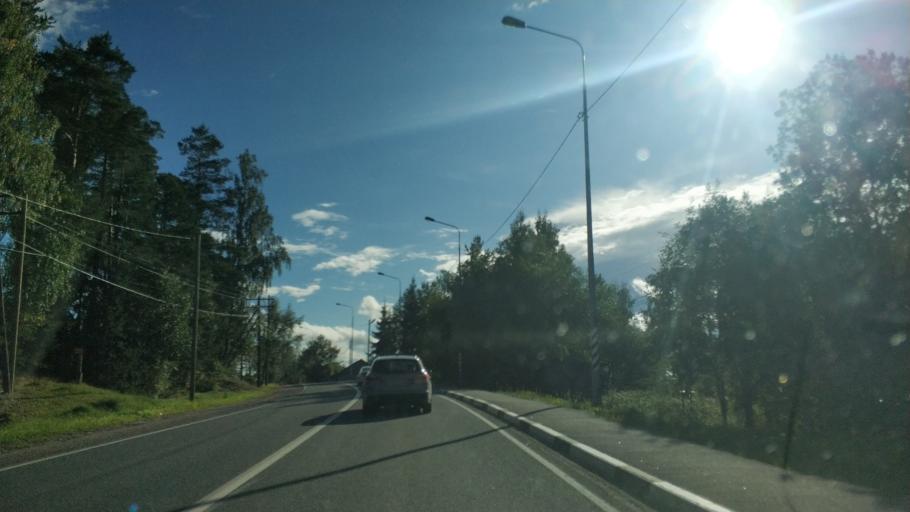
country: RU
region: Republic of Karelia
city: Lakhdenpokh'ya
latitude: 61.5293
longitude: 30.2047
